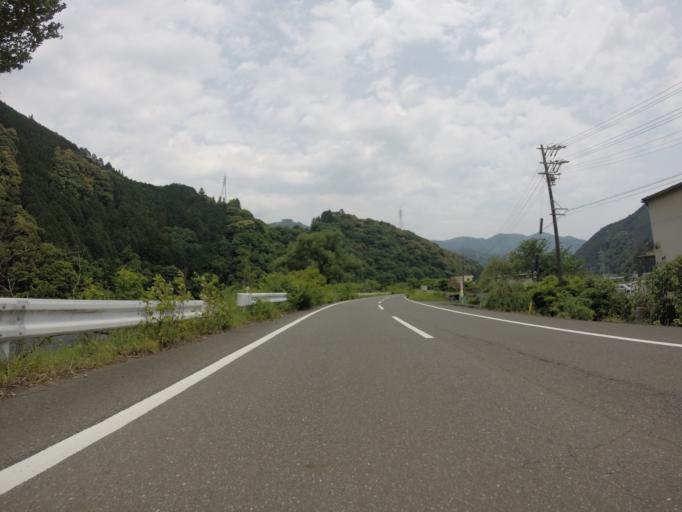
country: JP
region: Shizuoka
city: Shizuoka-shi
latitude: 35.1160
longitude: 138.3489
